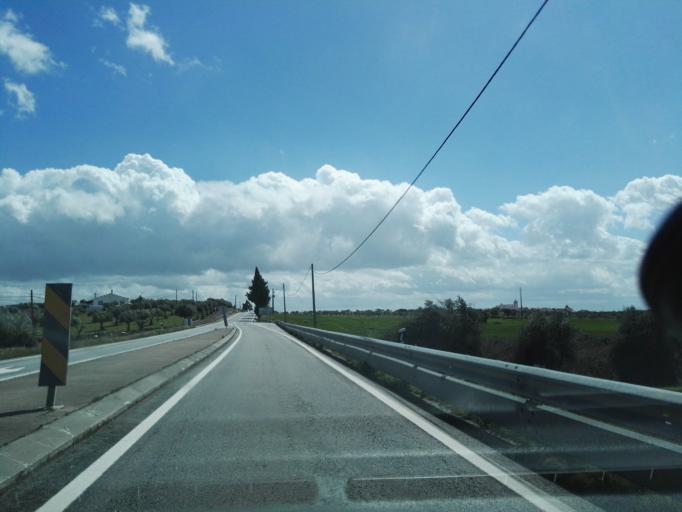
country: PT
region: Portalegre
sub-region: Arronches
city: Arronches
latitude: 39.1340
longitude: -7.2901
